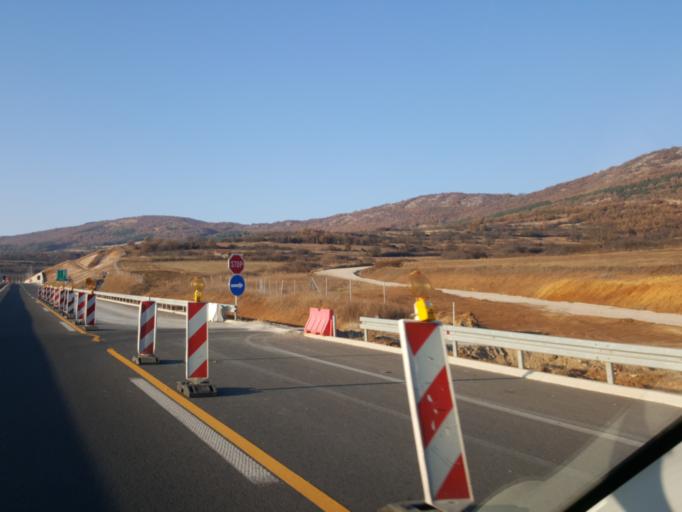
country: RS
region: Central Serbia
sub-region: Pirotski Okrug
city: Dimitrovgrad
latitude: 43.0175
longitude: 22.7995
